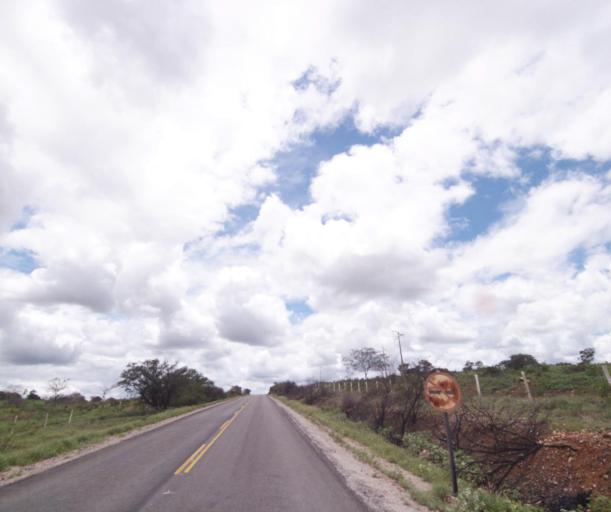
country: BR
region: Bahia
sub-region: Brumado
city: Brumado
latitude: -14.1530
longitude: -41.5122
